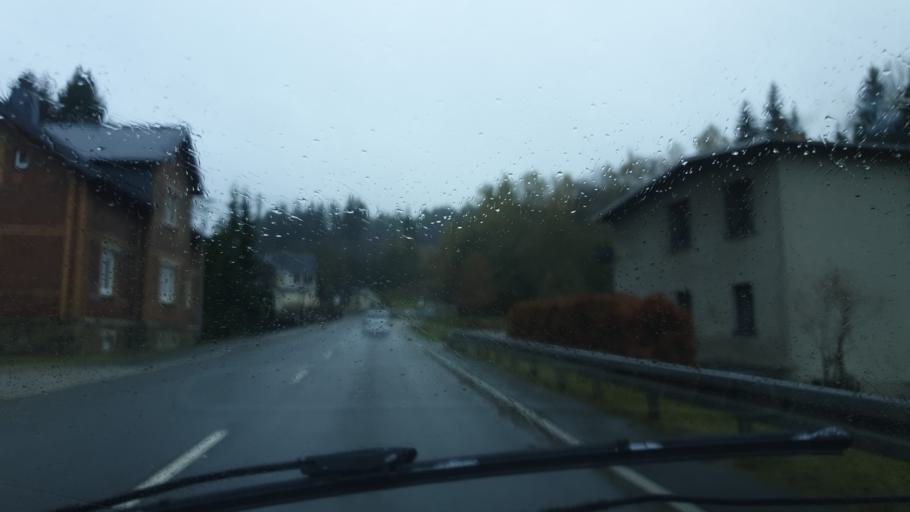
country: DE
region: Saxony
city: Tannenbergsthal
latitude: 50.4302
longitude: 12.4708
